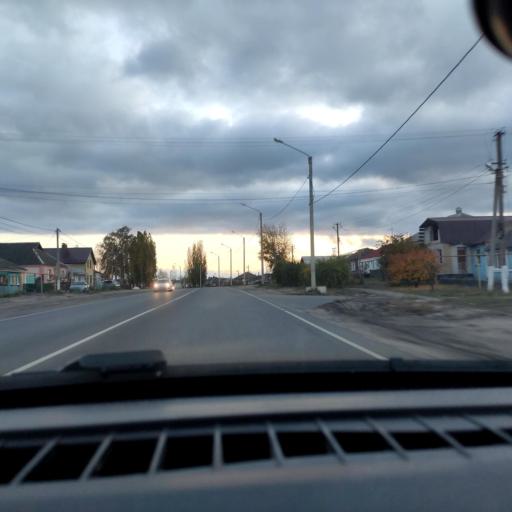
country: RU
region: Voronezj
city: Pridonskoy
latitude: 51.7104
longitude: 39.0741
